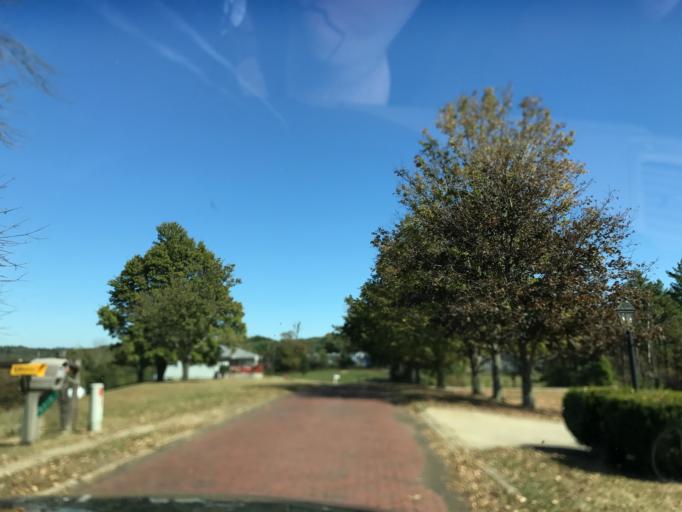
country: US
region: Ohio
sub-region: Muskingum County
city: New Concord
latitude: 39.9818
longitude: -81.8031
